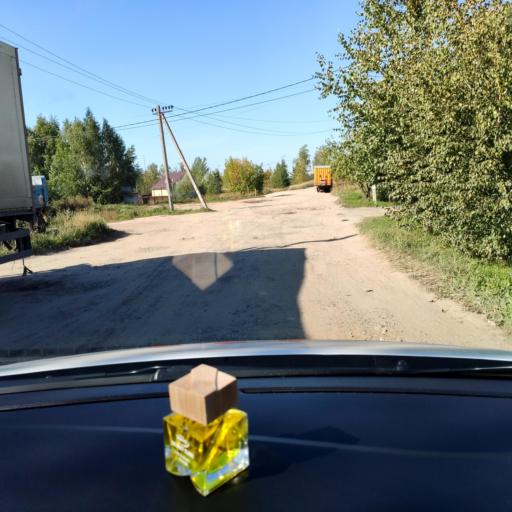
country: RU
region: Tatarstan
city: Vysokaya Gora
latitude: 55.8799
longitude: 49.2478
